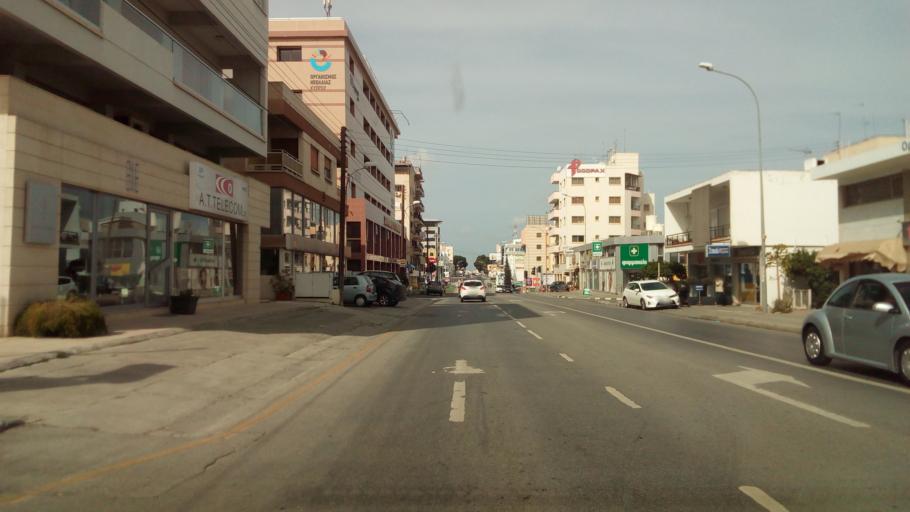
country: CY
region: Lefkosia
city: Nicosia
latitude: 35.1440
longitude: 33.3640
